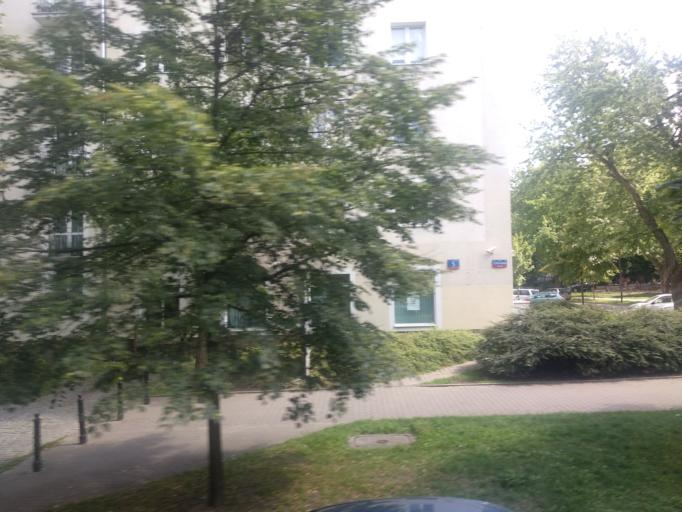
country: PL
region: Masovian Voivodeship
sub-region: Warszawa
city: Wola
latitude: 52.2517
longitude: 20.9946
